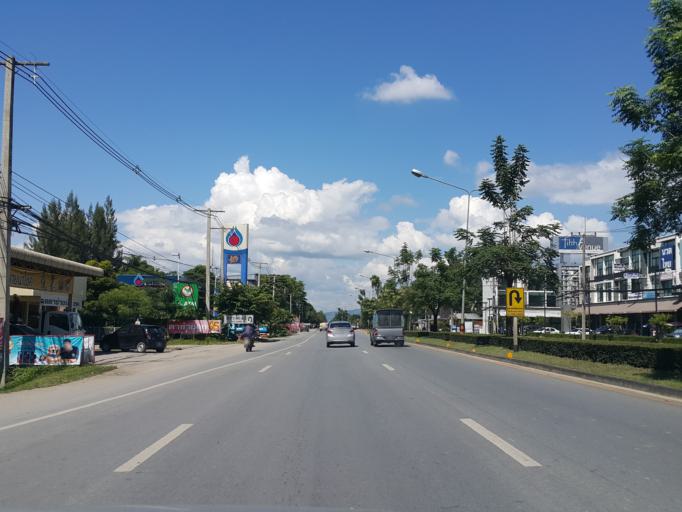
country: TH
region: Chiang Mai
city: San Sai
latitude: 18.8278
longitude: 99.0122
